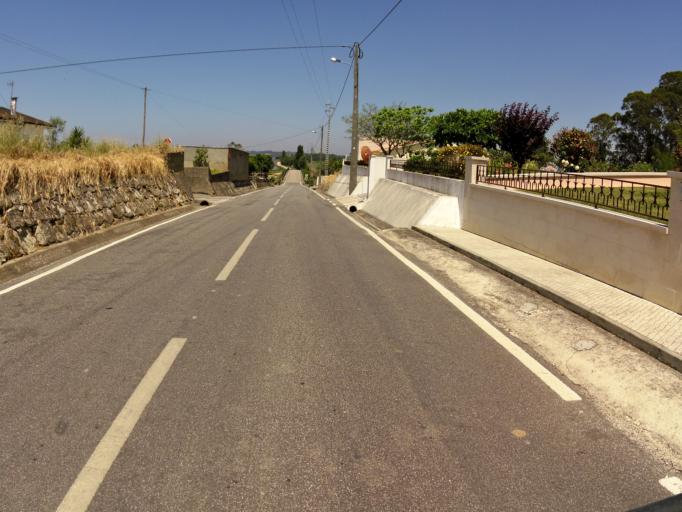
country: PT
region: Coimbra
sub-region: Montemor-O-Velho
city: Montemor-o-Velho
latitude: 40.1585
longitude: -8.7135
